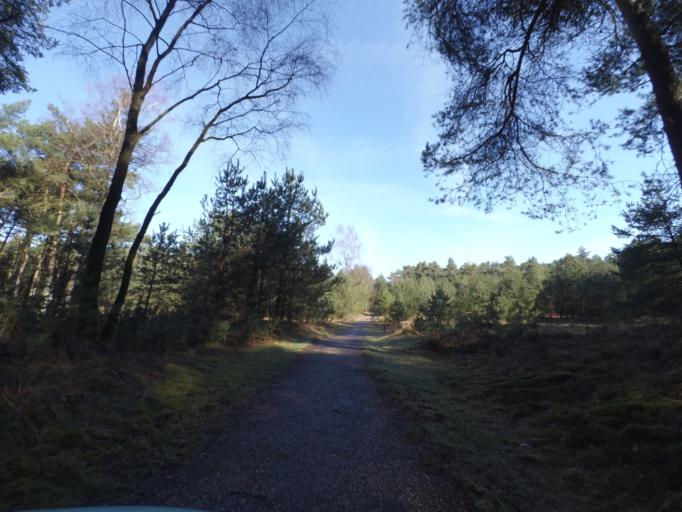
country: NL
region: Gelderland
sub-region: Gemeente Ede
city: Harskamp
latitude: 52.1585
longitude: 5.7346
